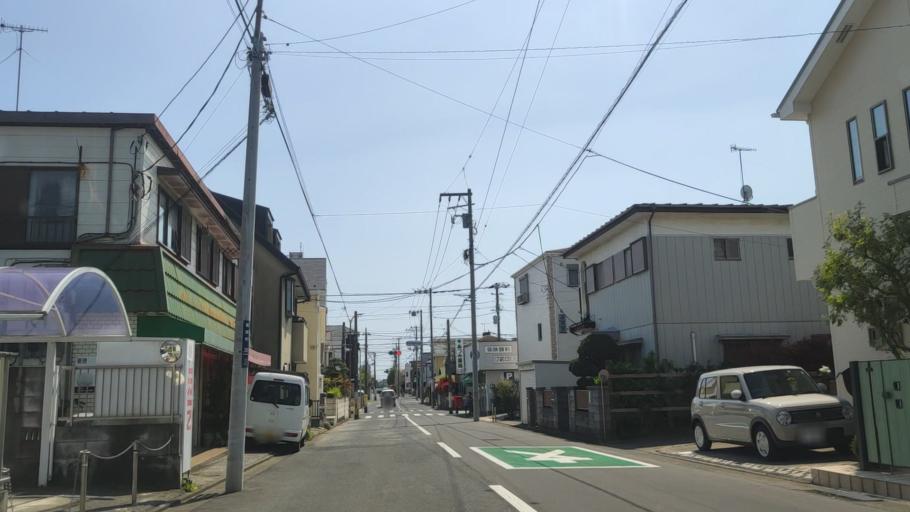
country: JP
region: Kanagawa
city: Hiratsuka
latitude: 35.3327
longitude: 139.3356
